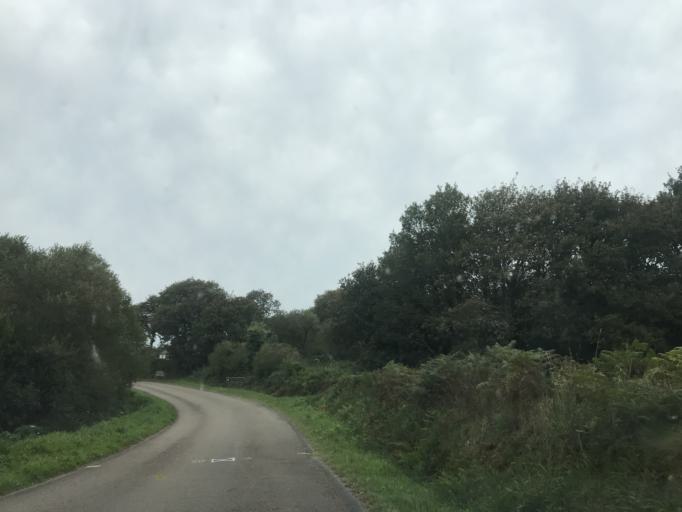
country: FR
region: Brittany
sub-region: Departement du Finistere
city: Plouneour-Menez
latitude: 48.3864
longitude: -3.9089
